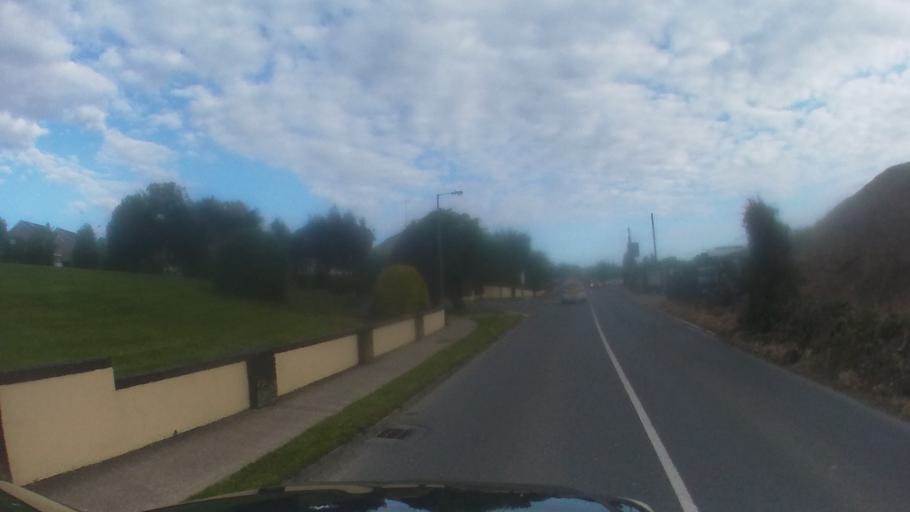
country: IE
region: Leinster
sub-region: Loch Garman
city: Gorey
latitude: 52.6780
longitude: -6.2859
